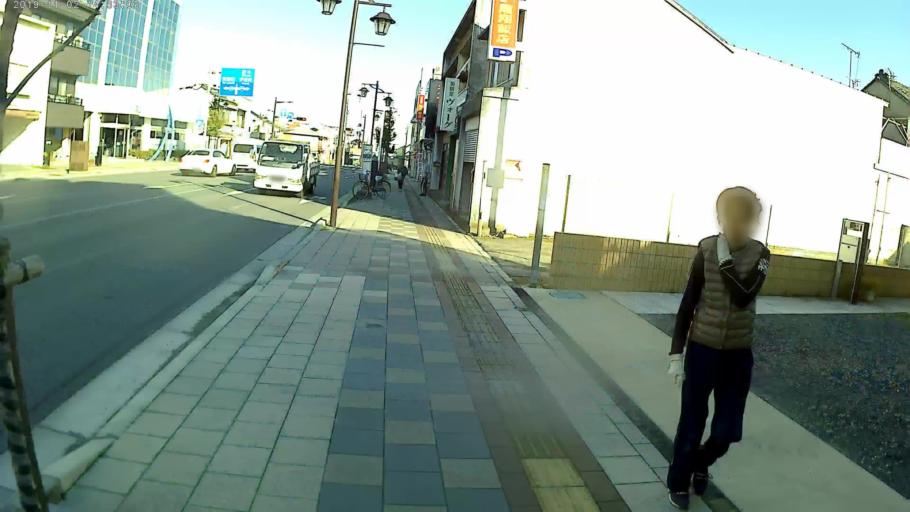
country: JP
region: Gunma
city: Takasaki
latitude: 36.3306
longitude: 139.0049
